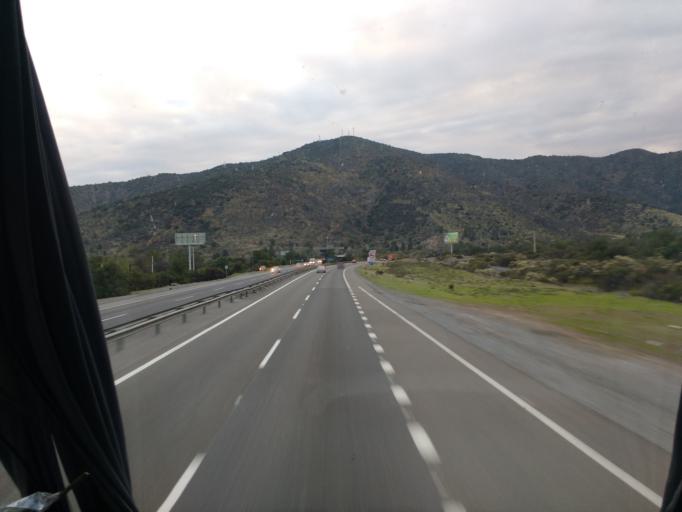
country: CL
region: Santiago Metropolitan
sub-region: Provincia de Talagante
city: Penaflor
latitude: -33.4577
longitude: -70.9242
